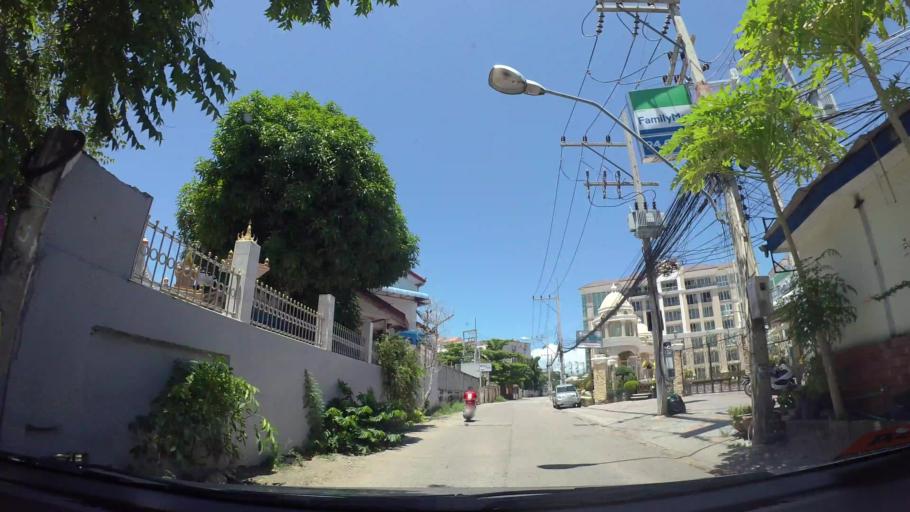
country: TH
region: Chon Buri
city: Phatthaya
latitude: 12.9286
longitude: 100.8950
